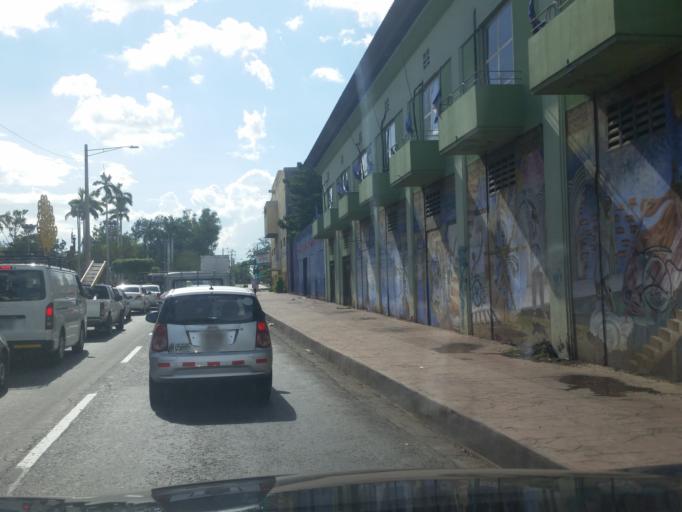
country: NI
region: Managua
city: Managua
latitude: 12.1547
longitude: -86.2727
